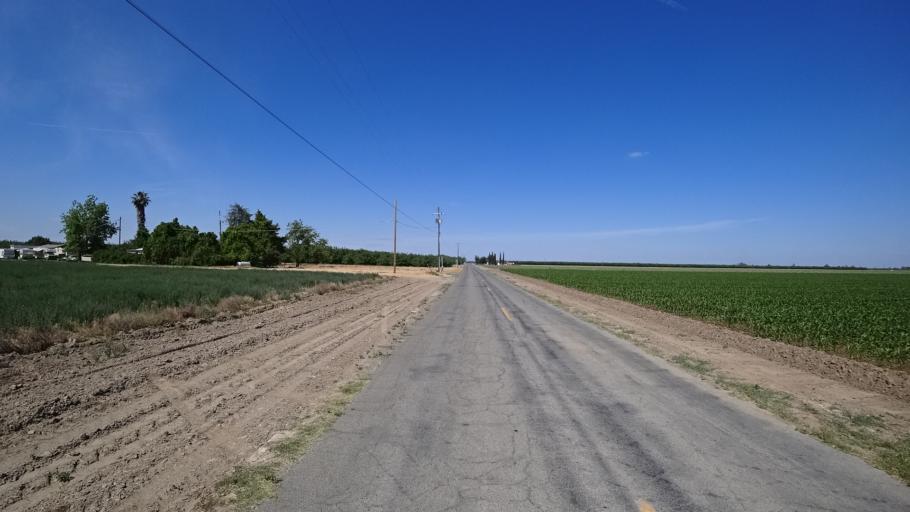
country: US
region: California
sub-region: Kings County
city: Armona
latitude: 36.2693
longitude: -119.6894
